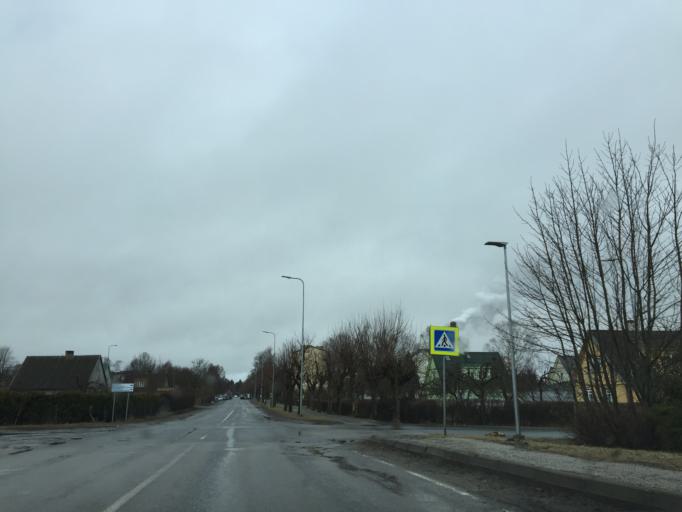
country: EE
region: Laeaene
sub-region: Haapsalu linn
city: Haapsalu
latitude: 58.9328
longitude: 23.5434
